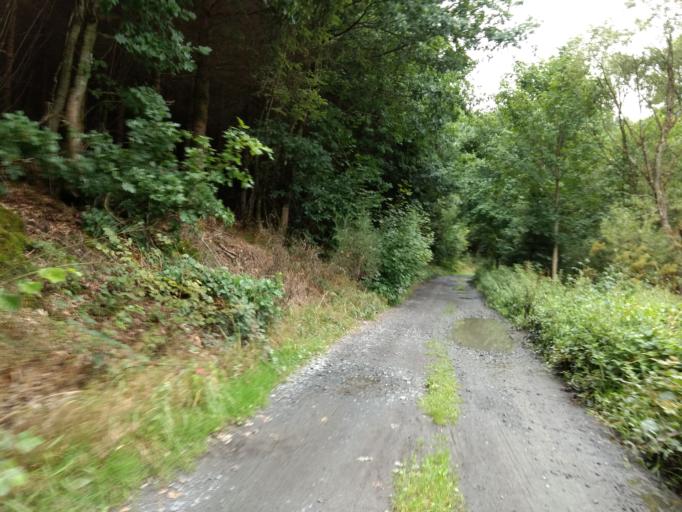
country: BE
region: Wallonia
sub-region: Province du Luxembourg
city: Houffalize
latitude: 50.1391
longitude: 5.7257
